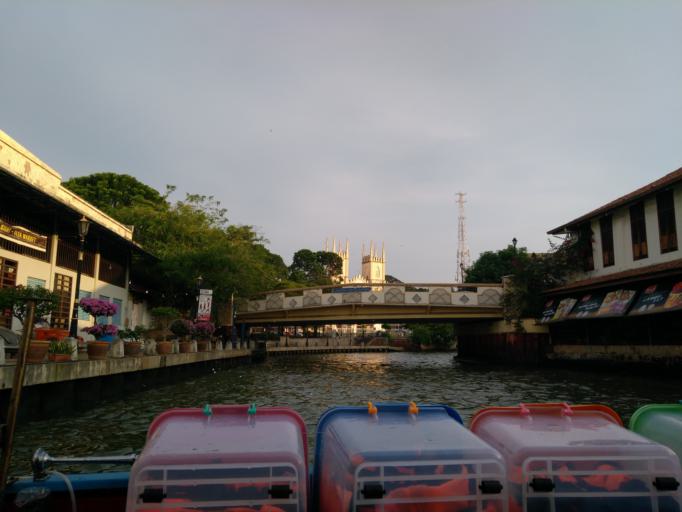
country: MY
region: Melaka
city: Malacca
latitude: 2.1967
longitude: 102.2506
